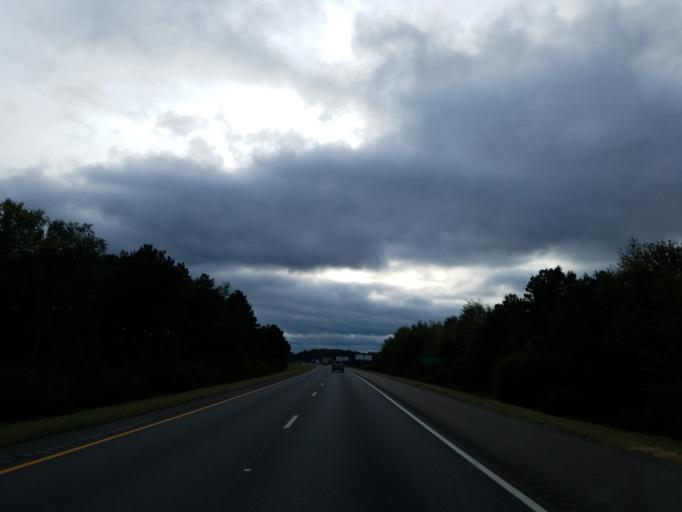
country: US
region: Alabama
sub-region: Tuscaloosa County
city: Tuscaloosa
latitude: 33.1489
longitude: -87.6122
